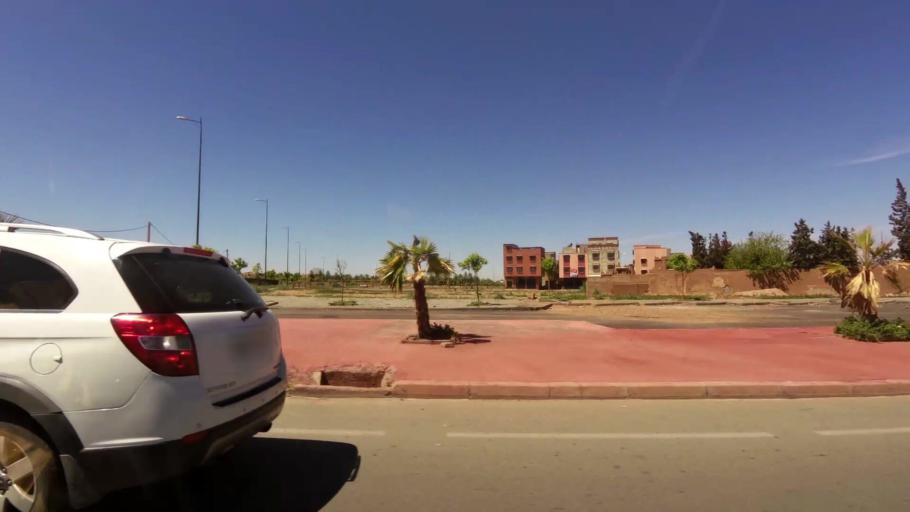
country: MA
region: Marrakech-Tensift-Al Haouz
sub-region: Marrakech
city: Marrakesh
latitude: 31.5585
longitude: -7.9771
